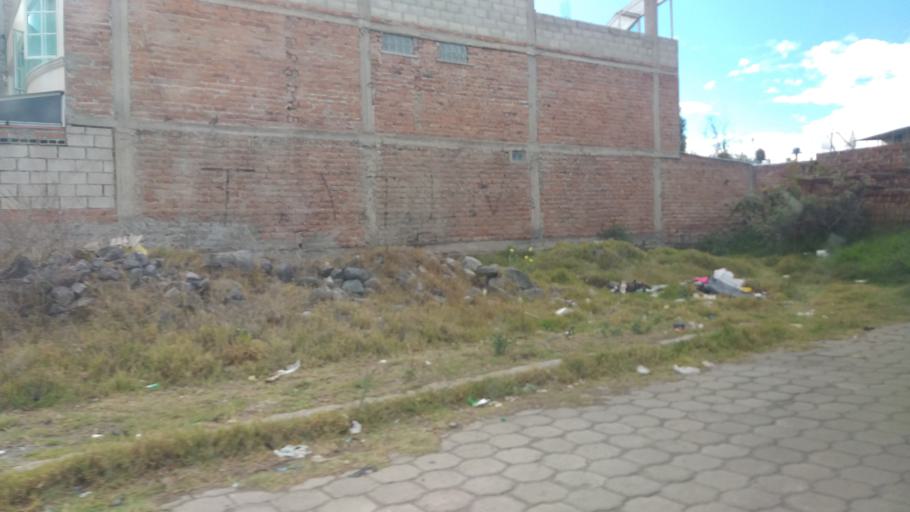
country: EC
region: Chimborazo
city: Riobamba
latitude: -1.6863
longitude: -78.6290
